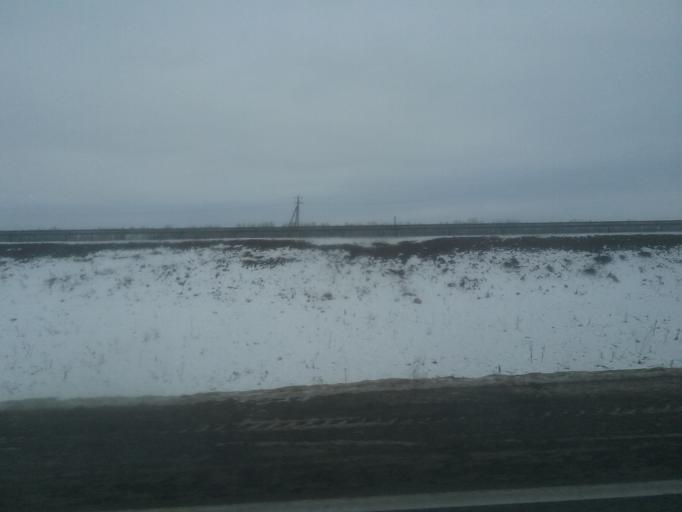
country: RU
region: Tula
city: Brusyanka
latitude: 54.0061
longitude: 38.0112
